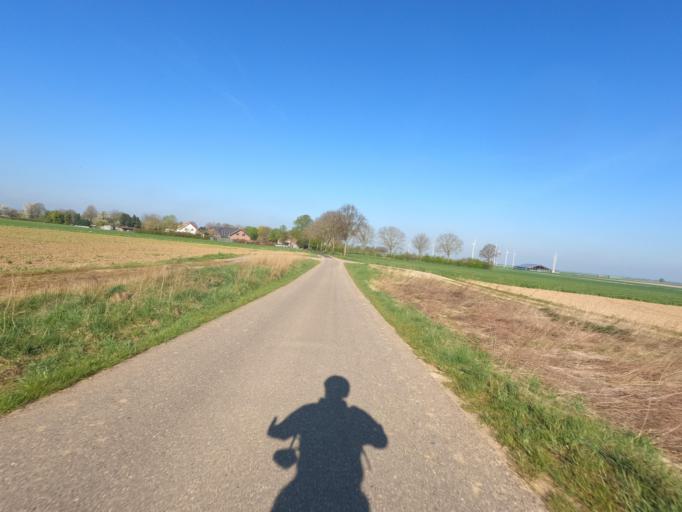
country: DE
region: North Rhine-Westphalia
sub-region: Regierungsbezirk Koln
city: Gangelt
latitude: 51.0183
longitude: 6.0503
